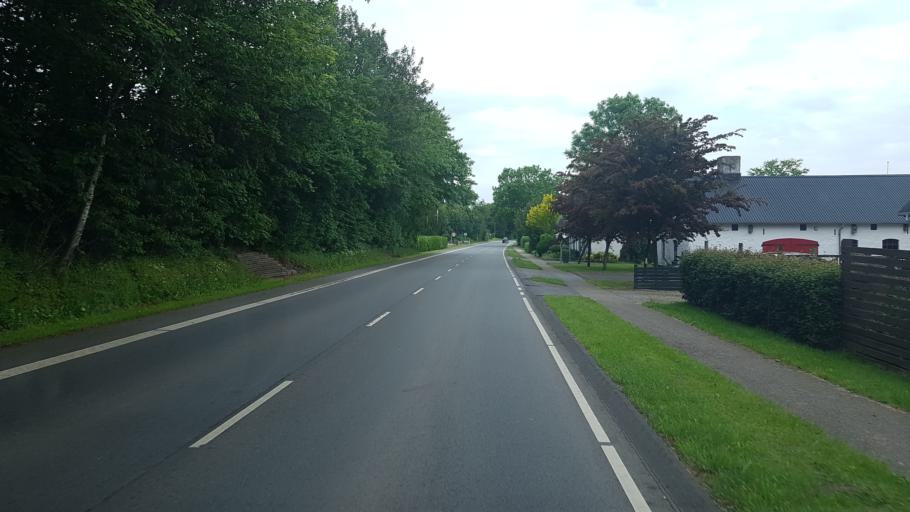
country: DK
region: South Denmark
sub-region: Vejen Kommune
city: Brorup
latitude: 55.4297
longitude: 9.0138
